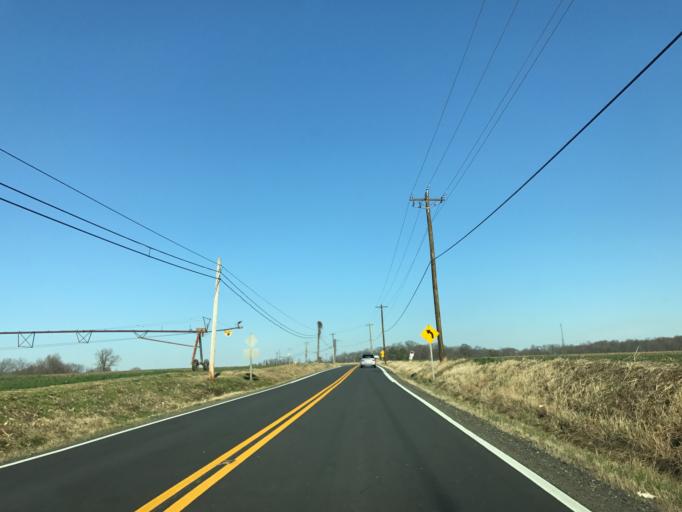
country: US
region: Maryland
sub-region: Queen Anne's County
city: Centreville
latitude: 39.0241
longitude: -76.1257
